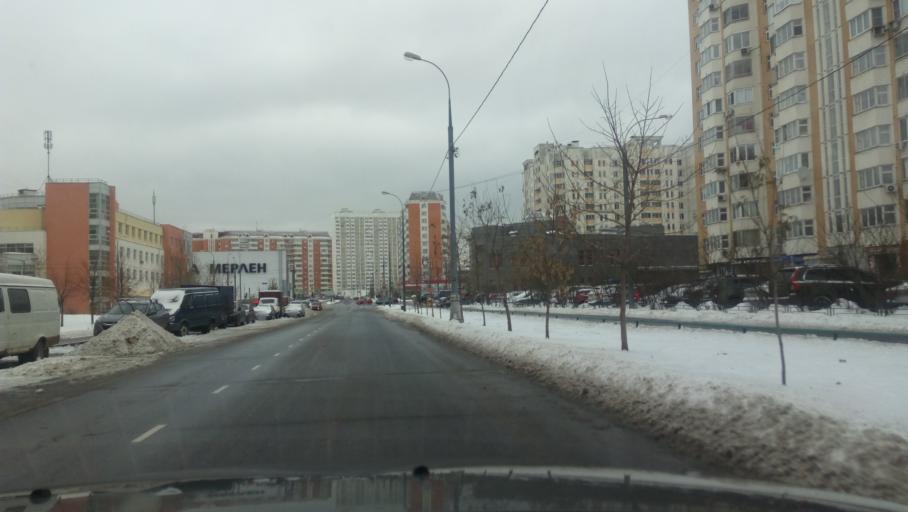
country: RU
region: Moscow
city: Nekrasovka
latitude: 55.7126
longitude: 37.8860
